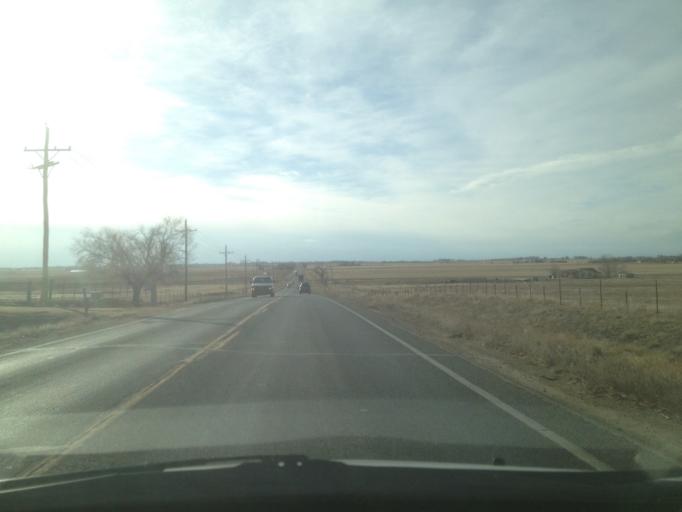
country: US
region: Colorado
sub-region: Weld County
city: Hudson
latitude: 40.0806
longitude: -104.6621
